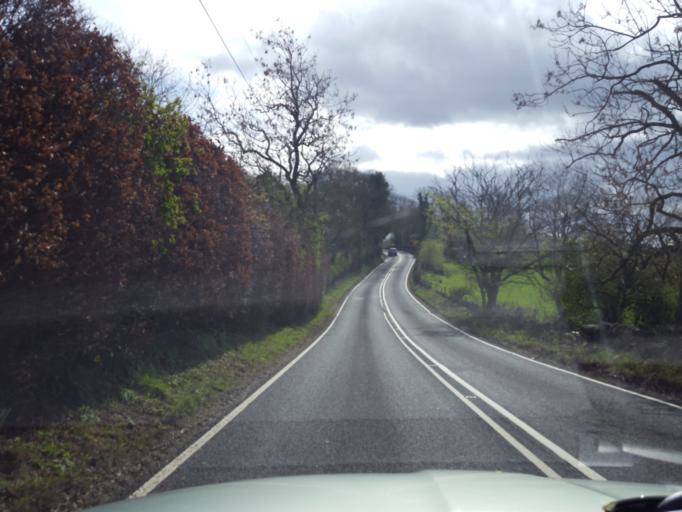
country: GB
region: Scotland
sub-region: West Lothian
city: Linlithgow
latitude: 55.9606
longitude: -3.6456
